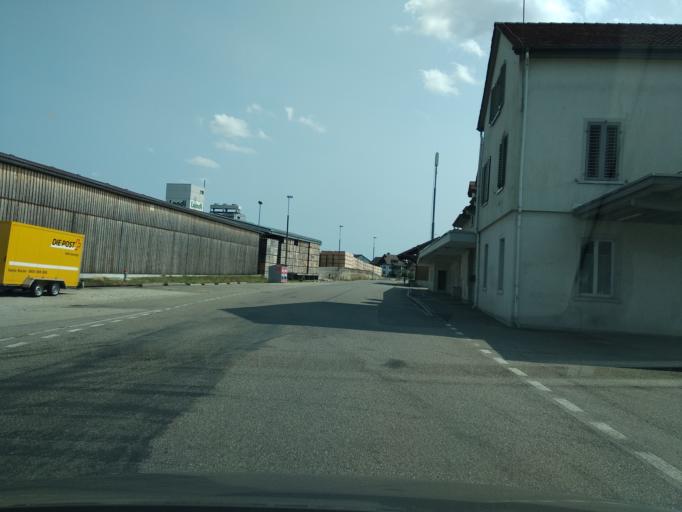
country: CH
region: Zurich
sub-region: Bezirk Andelfingen
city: Marthalen
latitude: 47.6353
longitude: 8.6529
